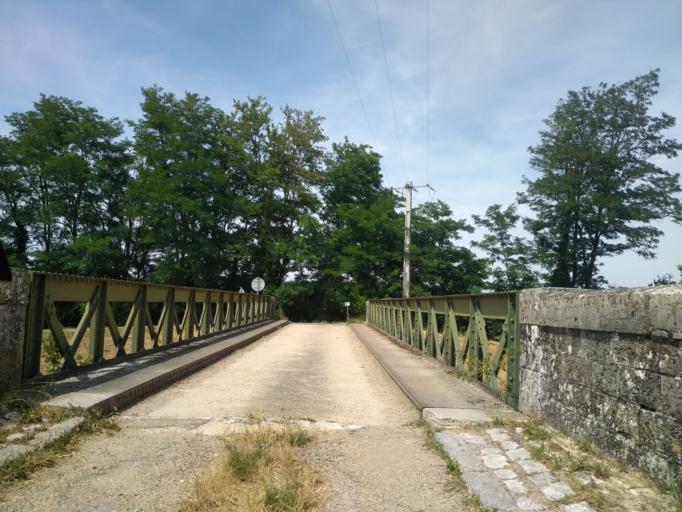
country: FR
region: Auvergne
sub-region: Departement de l'Allier
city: Molinet
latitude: 46.4778
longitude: 3.9131
